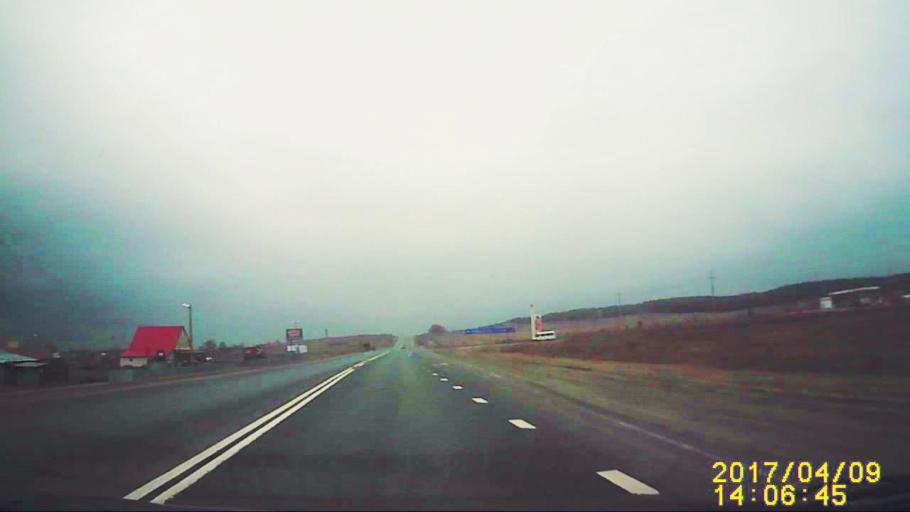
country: RU
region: Ulyanovsk
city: Silikatnyy
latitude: 54.0049
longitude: 48.2205
